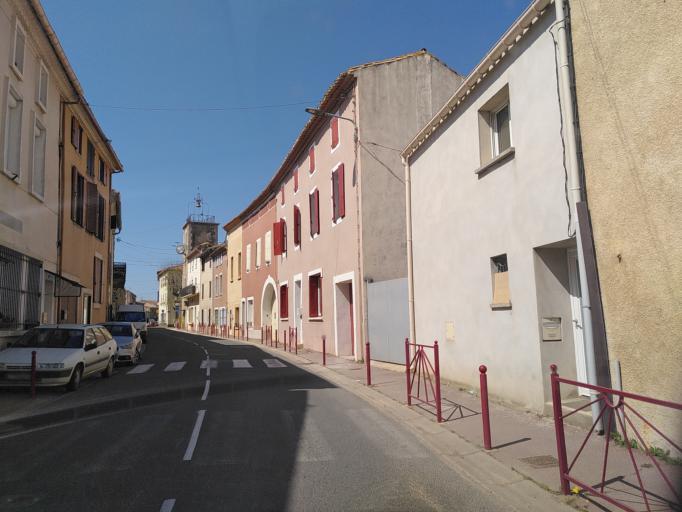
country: FR
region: Languedoc-Roussillon
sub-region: Departement de l'Aude
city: Ferrals-les-Corbieres
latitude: 43.1033
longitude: 2.7717
